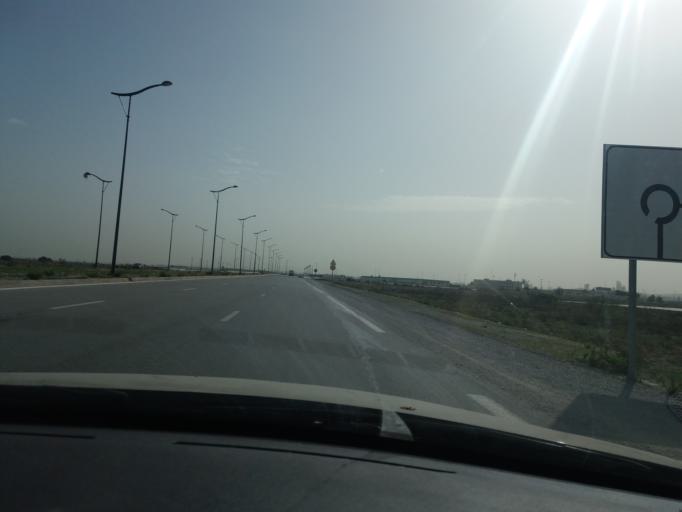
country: TN
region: Tunis
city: Tunis
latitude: 36.8065
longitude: 10.1940
